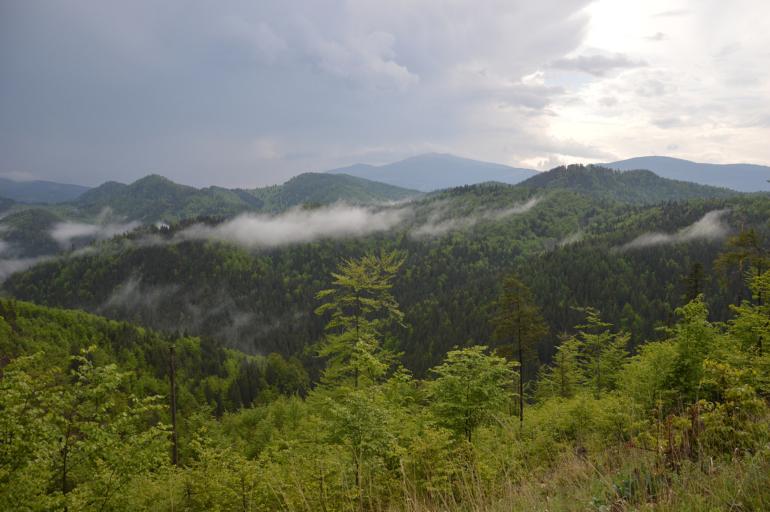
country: SK
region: Kosicky
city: Dobsina
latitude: 48.9011
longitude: 20.3132
